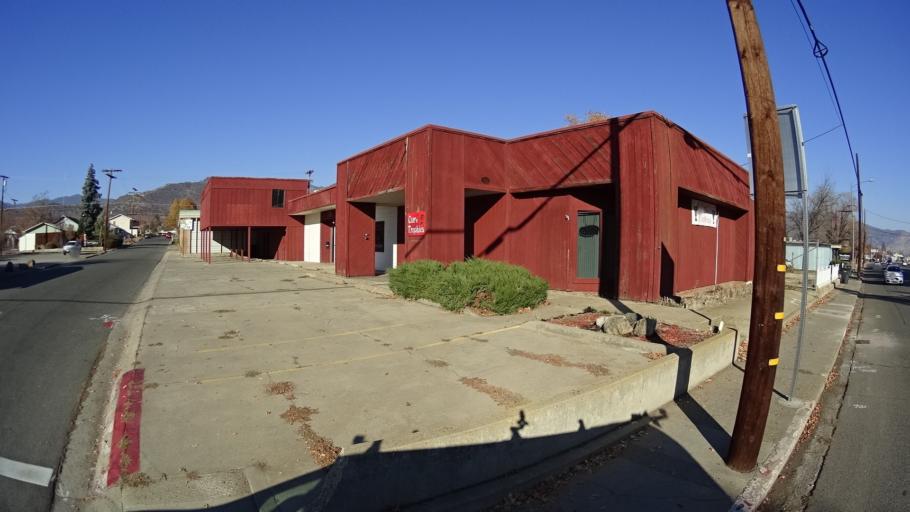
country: US
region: California
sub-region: Siskiyou County
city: Yreka
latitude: 41.7230
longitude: -122.6392
